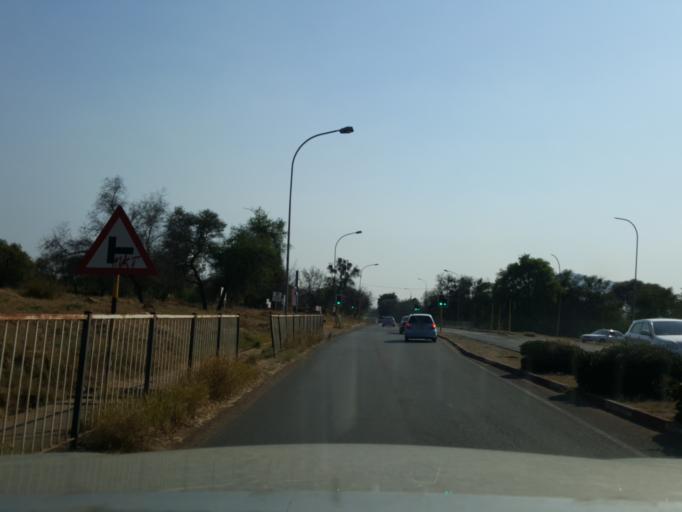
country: BW
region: South East
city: Lobatse
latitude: -25.2263
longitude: 25.6766
